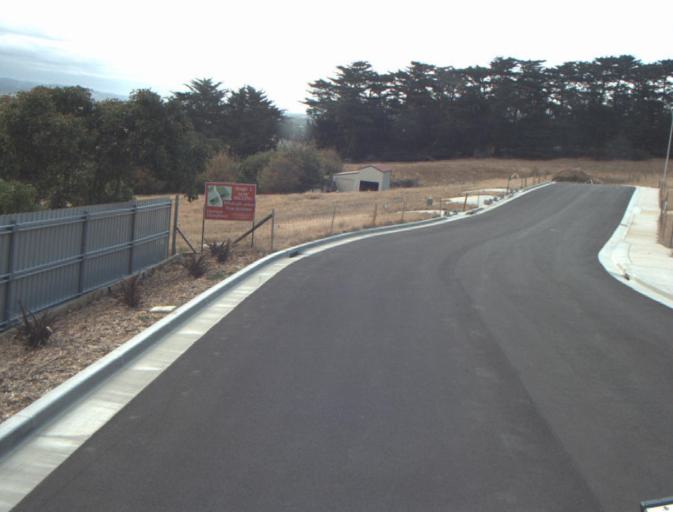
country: AU
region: Tasmania
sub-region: Launceston
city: Newstead
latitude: -41.4546
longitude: 147.2076
